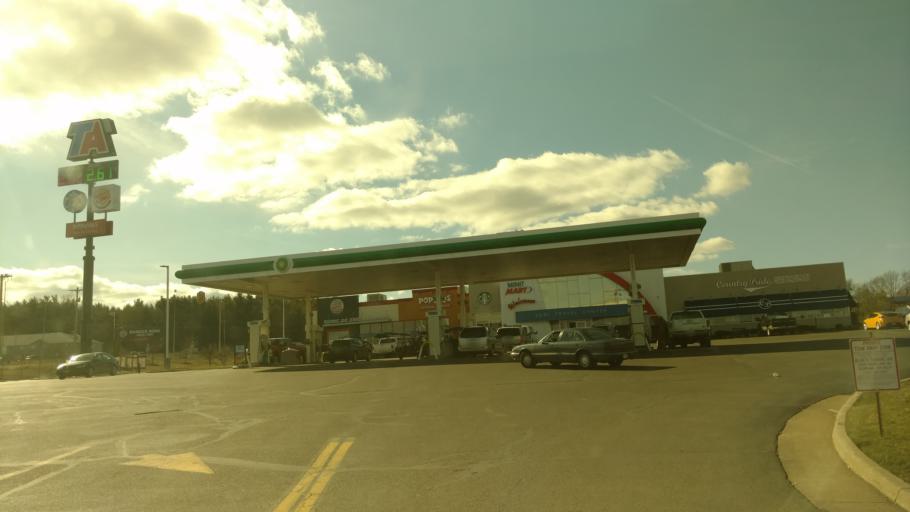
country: US
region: Ohio
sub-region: Medina County
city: Westfield Center
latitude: 41.0320
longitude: -81.9067
